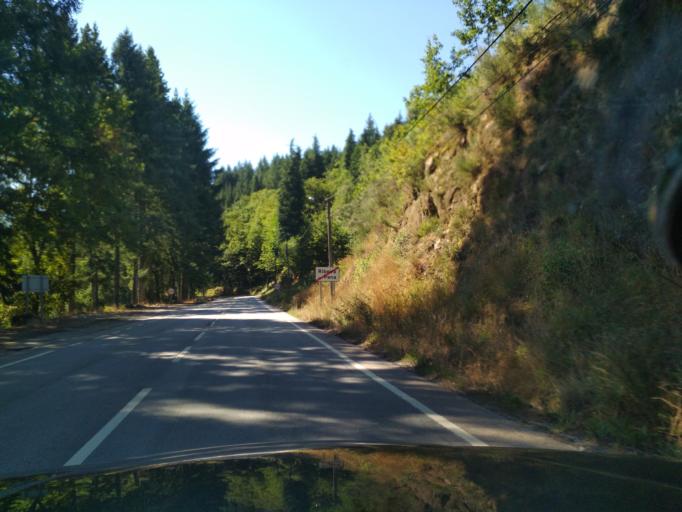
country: PT
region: Vila Real
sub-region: Ribeira de Pena
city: Ribeira de Pena
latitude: 41.5188
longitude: -7.8064
